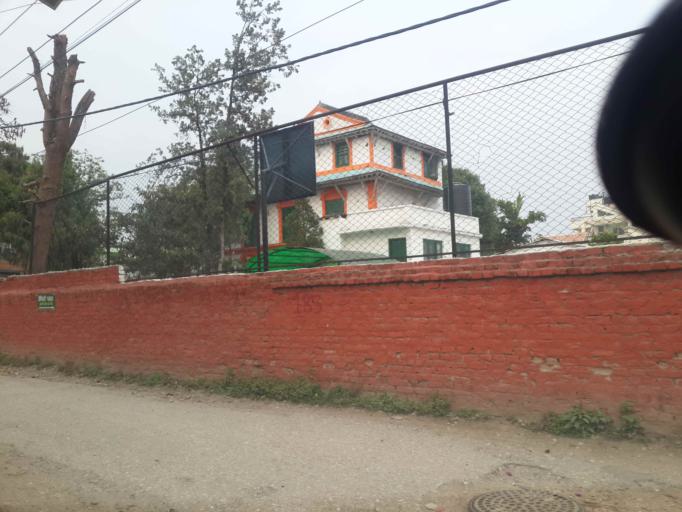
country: NP
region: Central Region
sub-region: Bagmati Zone
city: Patan
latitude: 27.6858
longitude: 85.3165
